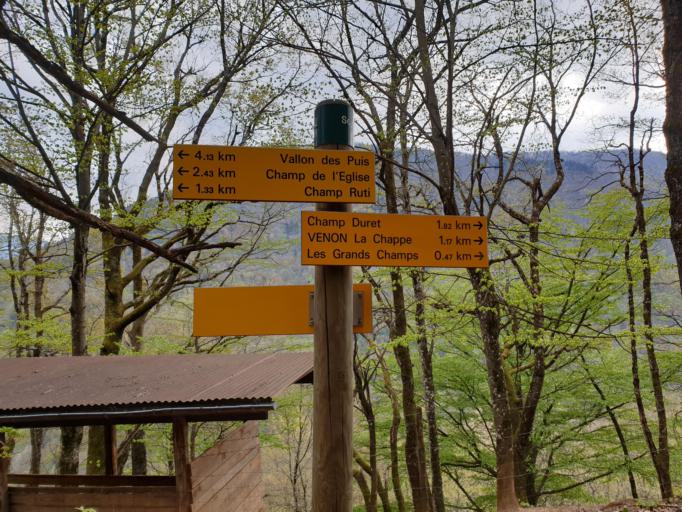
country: FR
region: Rhone-Alpes
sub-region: Departement de l'Isere
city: Gieres
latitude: 45.1665
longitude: 5.8127
